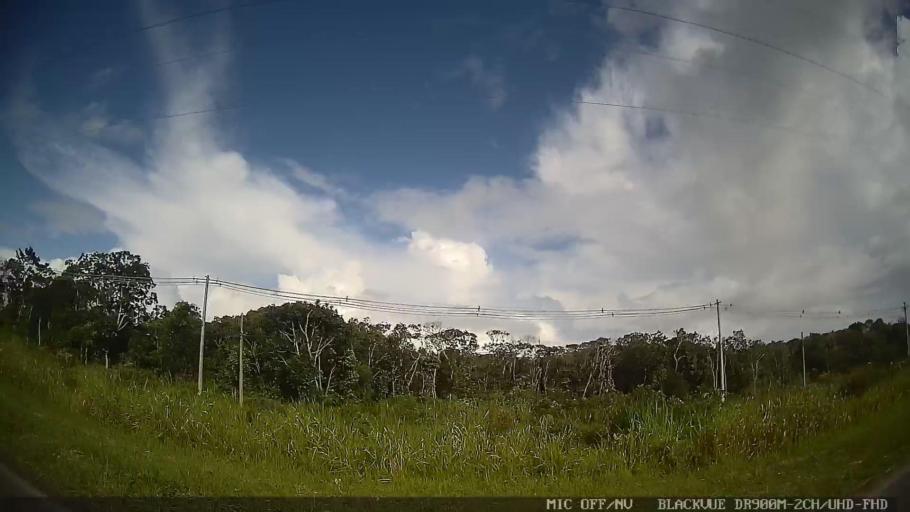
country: BR
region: Sao Paulo
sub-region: Peruibe
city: Peruibe
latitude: -24.2379
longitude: -46.9080
